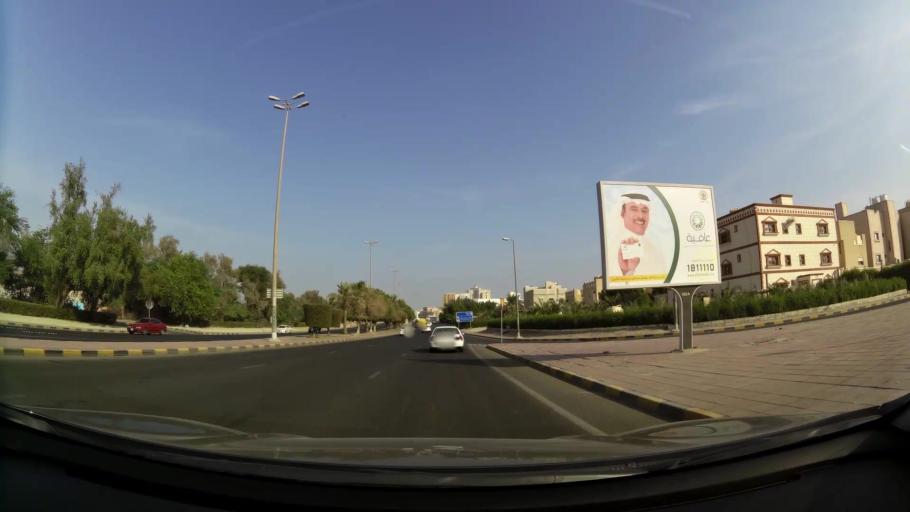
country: KW
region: Mubarak al Kabir
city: Mubarak al Kabir
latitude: 29.1748
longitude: 48.0886
